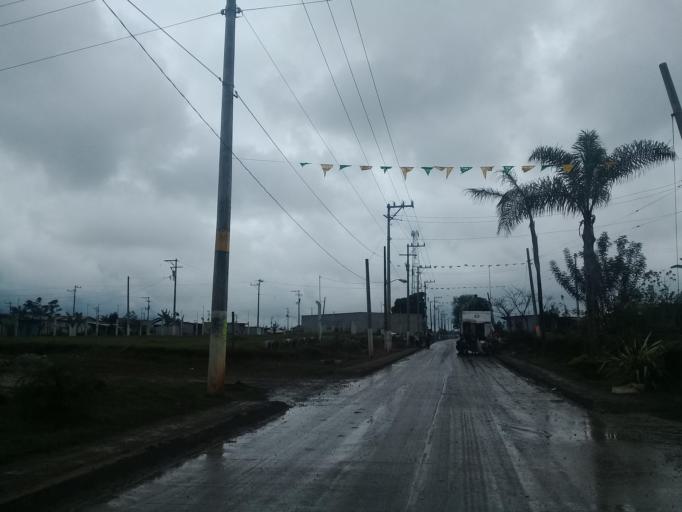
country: MX
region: Veracruz
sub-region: Cordoba
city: San Jose de Tapia
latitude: 18.8507
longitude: -96.9562
